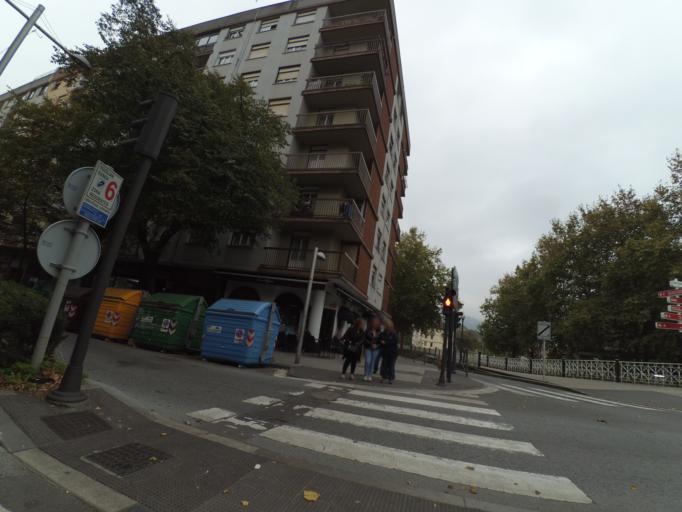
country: ES
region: Basque Country
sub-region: Provincia de Guipuzcoa
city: Irun
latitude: 43.3394
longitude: -1.7845
